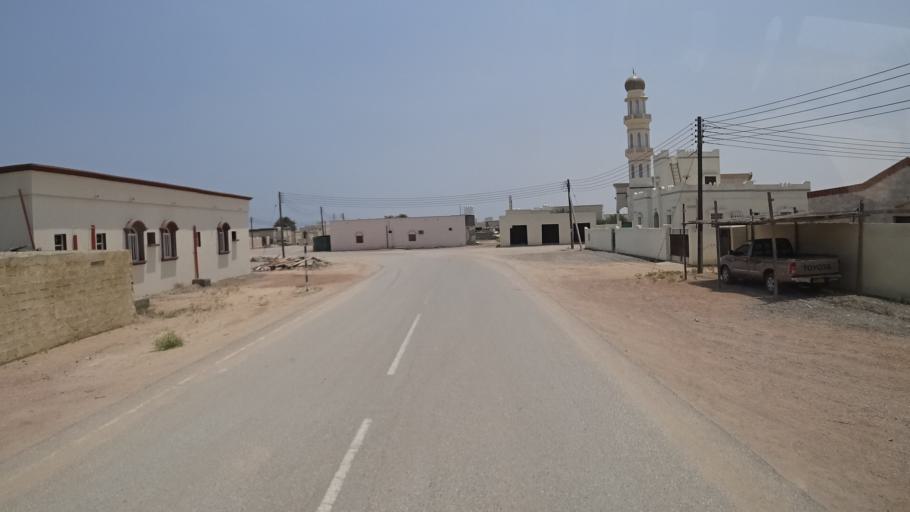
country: OM
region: Ash Sharqiyah
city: Sur
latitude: 22.5203
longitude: 59.7976
